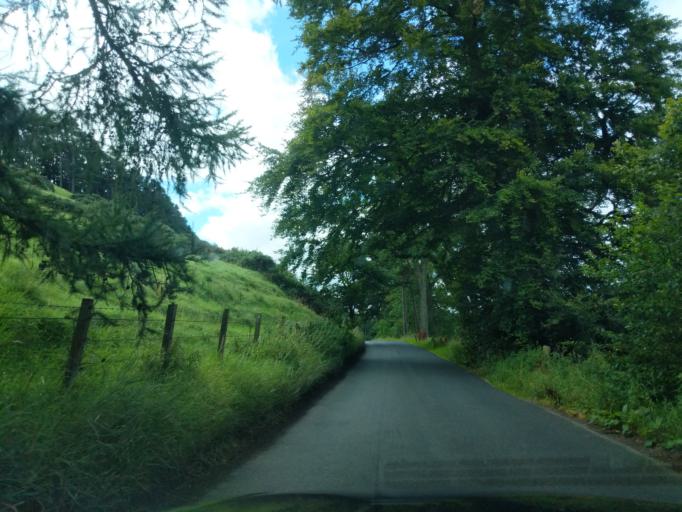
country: GB
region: Scotland
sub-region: The Scottish Borders
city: West Linton
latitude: 55.7100
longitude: -3.3351
